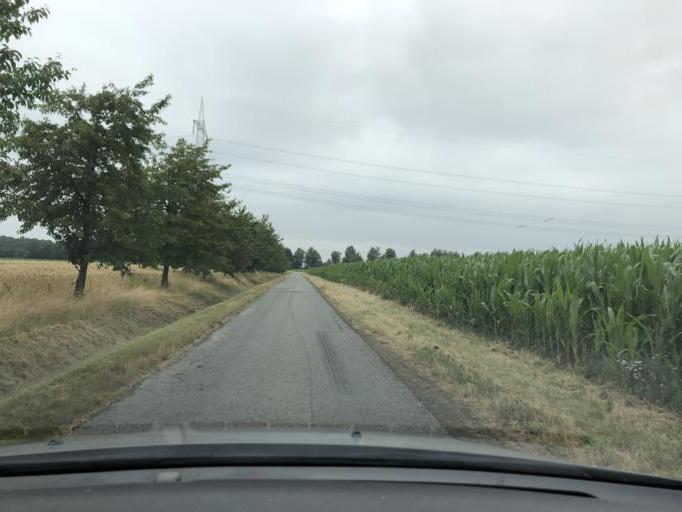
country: DE
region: Saxony
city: Frohburg
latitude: 51.1095
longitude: 12.5654
